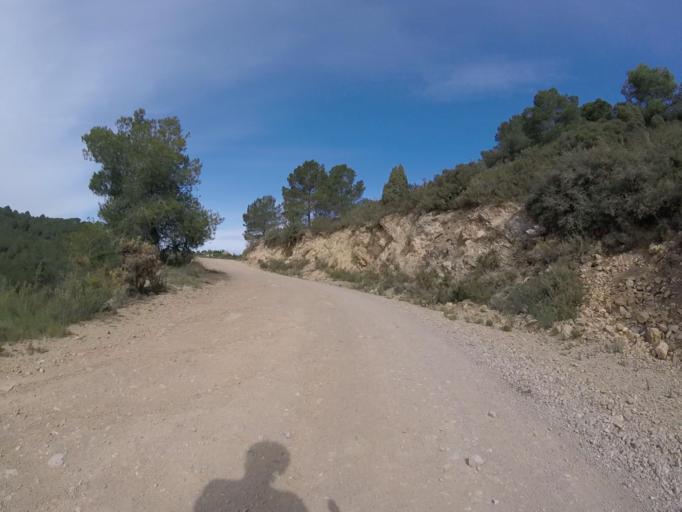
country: ES
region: Valencia
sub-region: Provincia de Castello
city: Torreblanca
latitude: 40.2048
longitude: 0.1502
